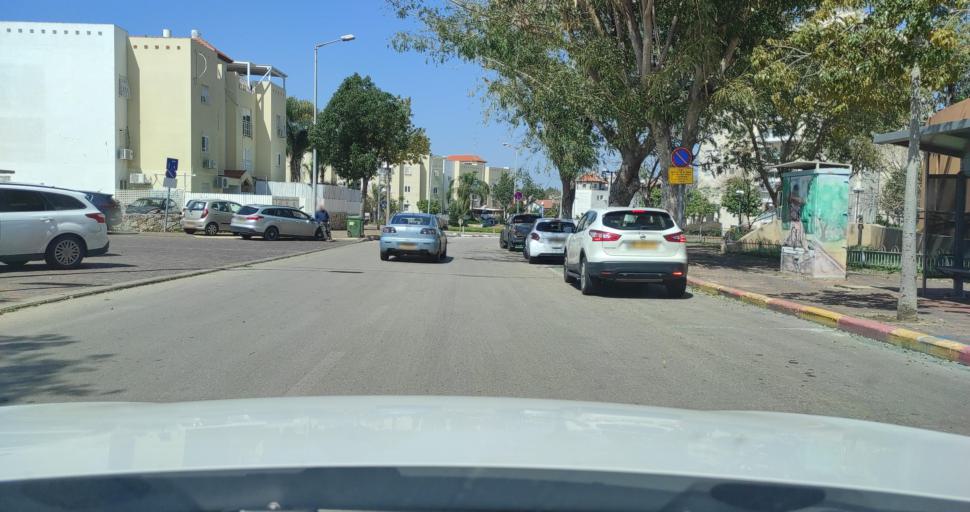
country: IL
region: Central District
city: Nordiyya
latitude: 32.3059
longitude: 34.8828
